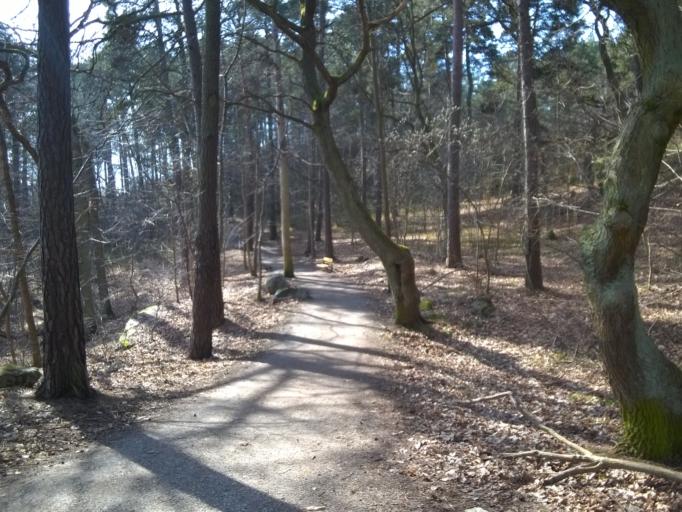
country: SE
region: Stockholm
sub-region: Sundbybergs Kommun
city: Sundbyberg
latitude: 59.3268
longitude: 17.9840
